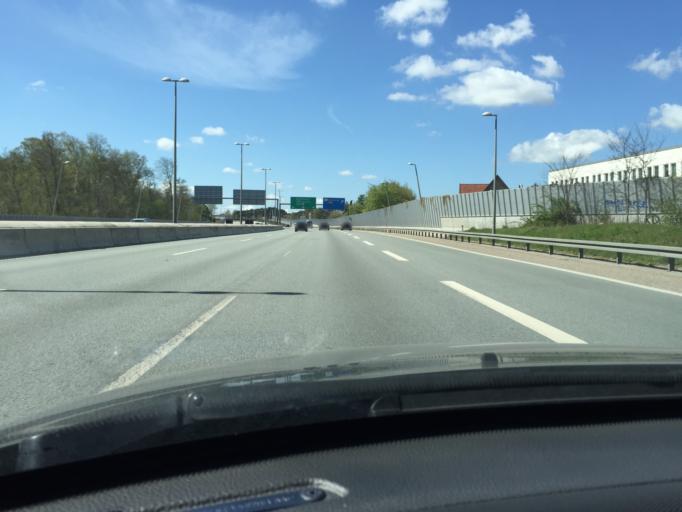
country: DK
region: Capital Region
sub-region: Lyngby-Tarbaek Kommune
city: Kongens Lyngby
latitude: 55.7569
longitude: 12.5031
